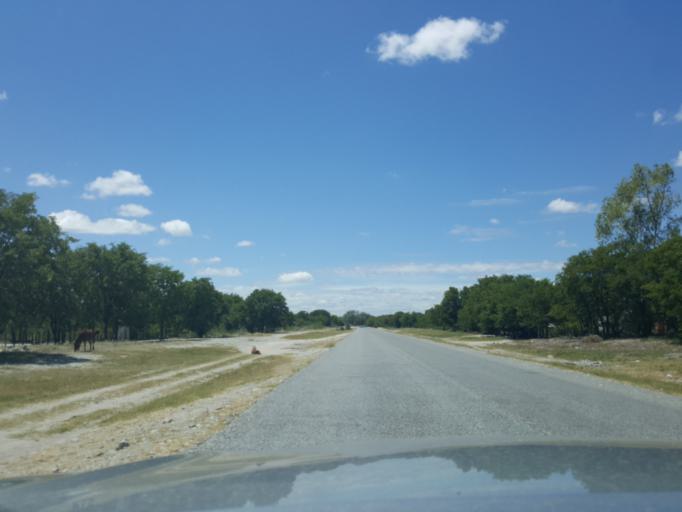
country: BW
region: Central
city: Nata
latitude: -20.2129
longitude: 26.1727
